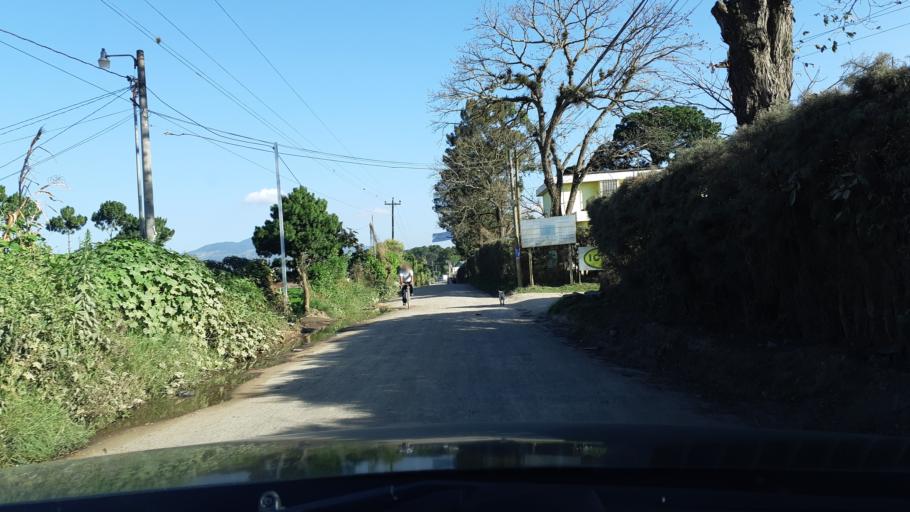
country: GT
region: Chimaltenango
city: El Tejar
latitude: 14.6385
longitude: -90.8039
